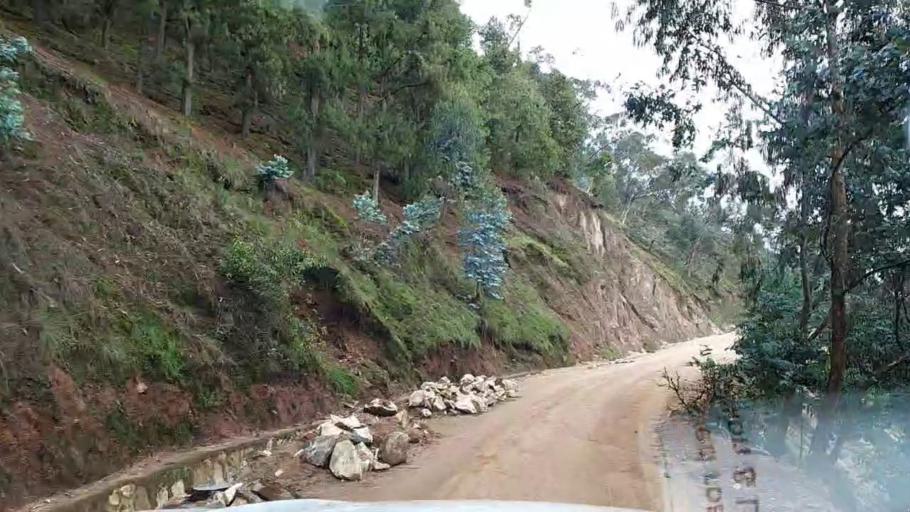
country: RW
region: Southern Province
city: Nzega
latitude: -2.3840
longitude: 29.4498
